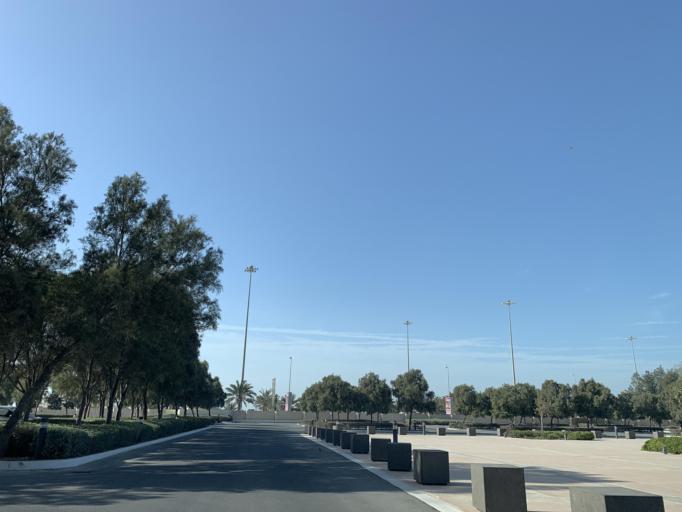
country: BH
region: Muharraq
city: Al Muharraq
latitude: 26.2423
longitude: 50.5971
